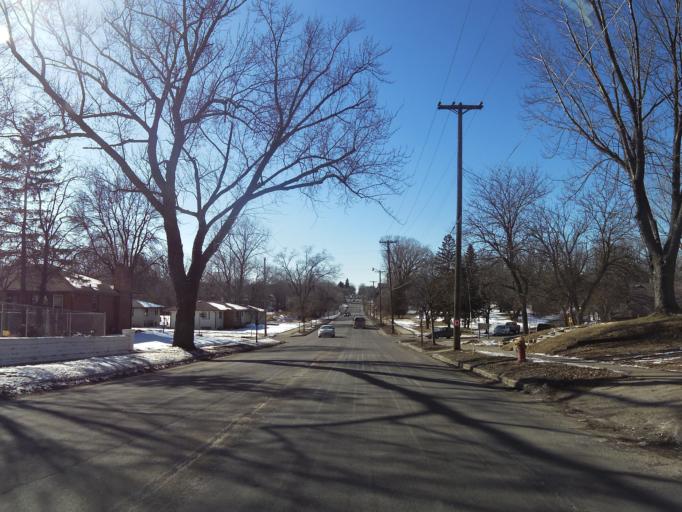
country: US
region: Minnesota
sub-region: Ramsey County
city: Saint Paul
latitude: 44.9568
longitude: -93.0492
